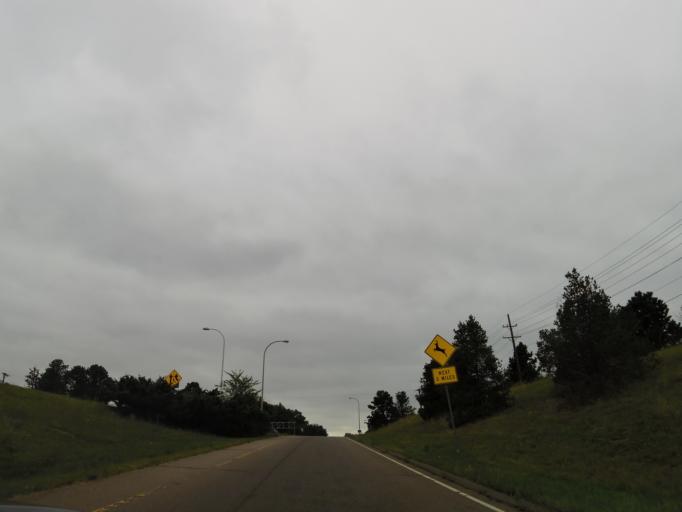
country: US
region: Colorado
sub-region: El Paso County
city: Colorado Springs
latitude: 38.7953
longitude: -104.8227
